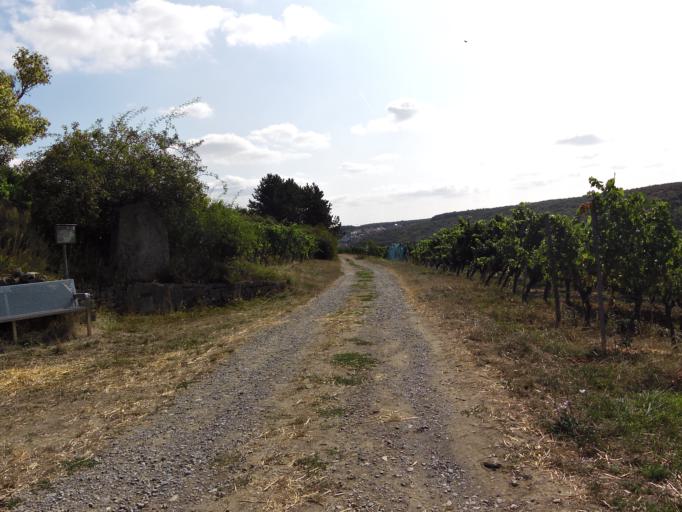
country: DE
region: Bavaria
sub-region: Regierungsbezirk Unterfranken
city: Gerbrunn
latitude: 49.7561
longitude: 10.0067
